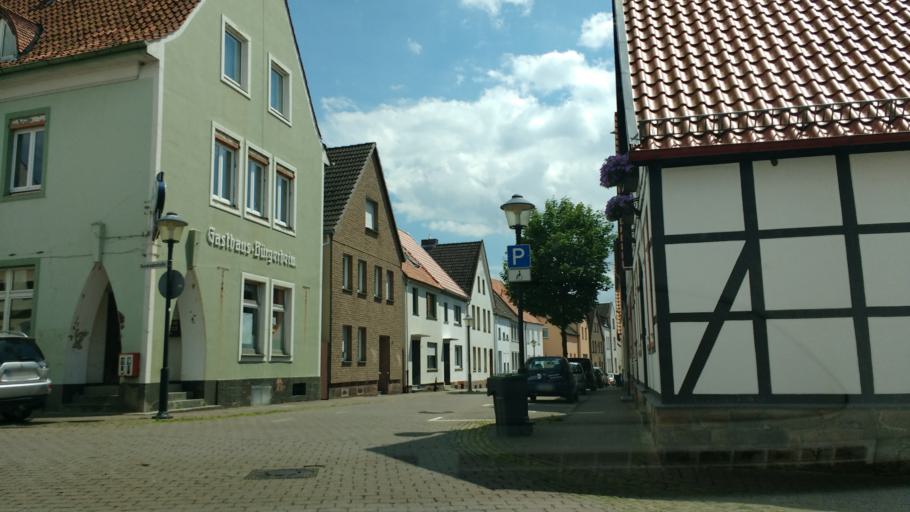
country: DE
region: North Rhine-Westphalia
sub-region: Regierungsbezirk Detmold
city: Blomberg
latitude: 51.9452
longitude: 9.0931
